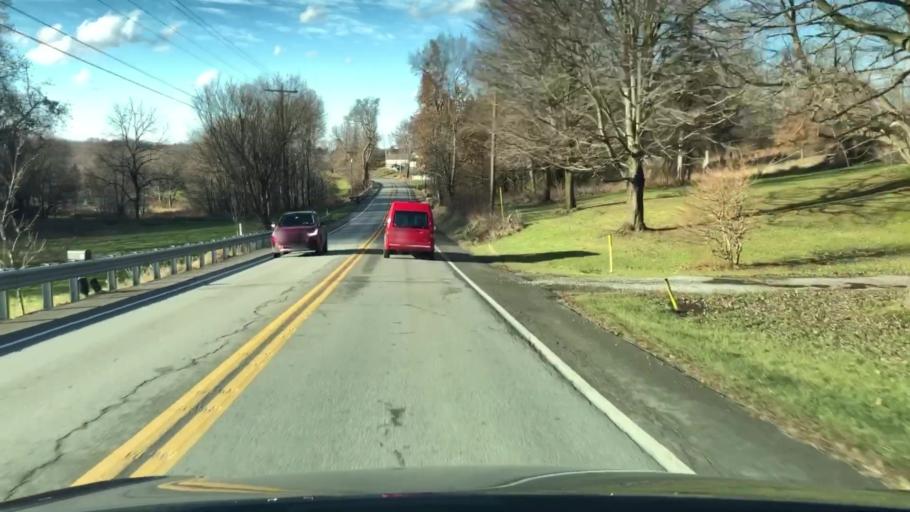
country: US
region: Pennsylvania
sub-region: Butler County
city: Meadowood
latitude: 40.8158
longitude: -79.8464
